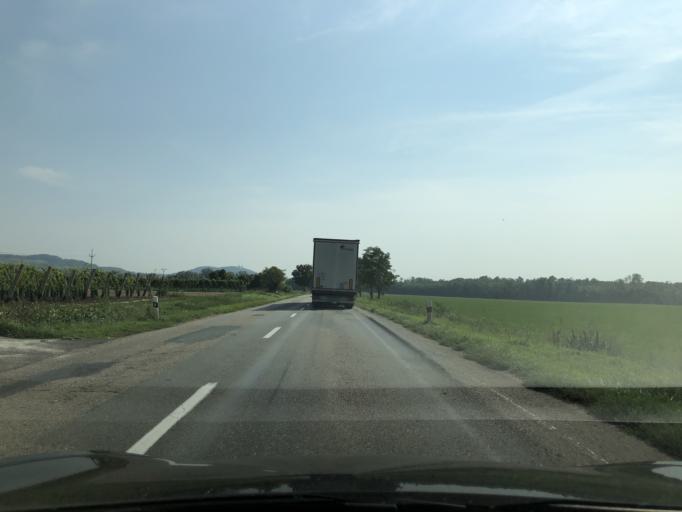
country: CZ
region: South Moravian
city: Brezi
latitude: 48.8195
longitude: 16.5821
